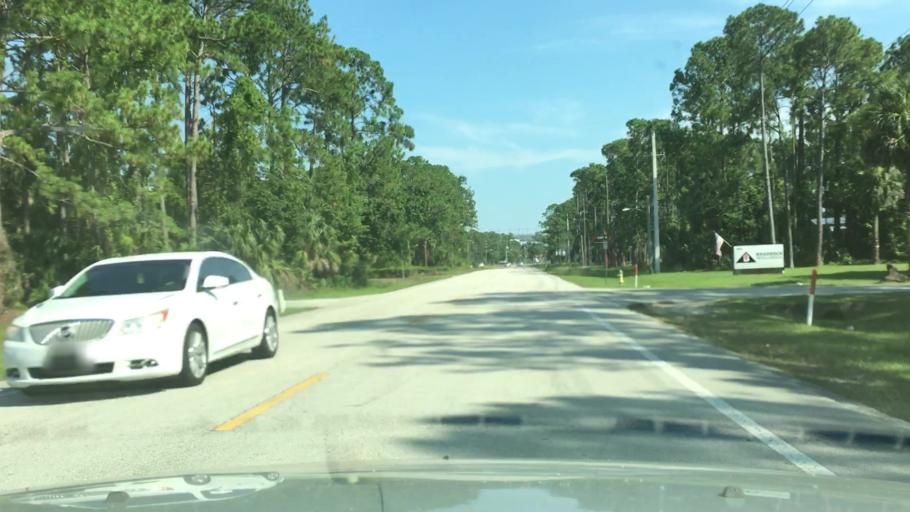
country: US
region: Florida
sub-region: Volusia County
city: Daytona Beach
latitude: 29.1971
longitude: -81.0807
